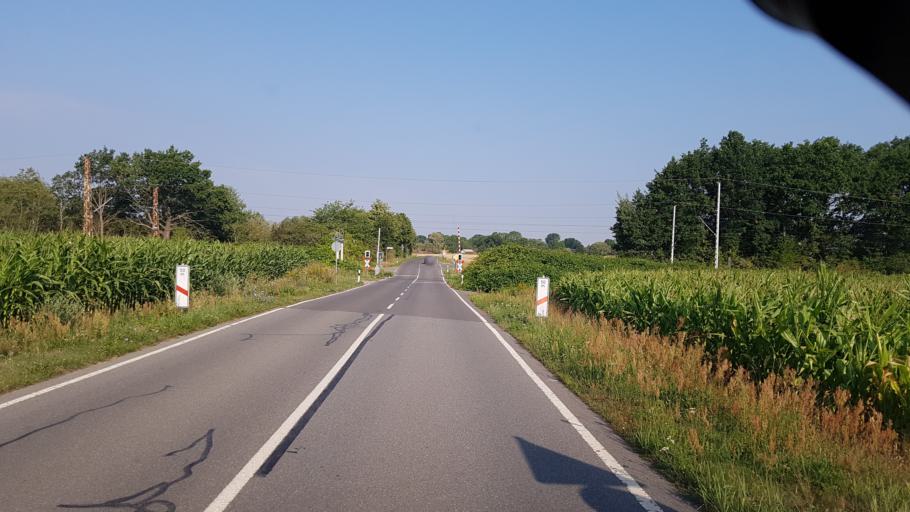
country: DE
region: Brandenburg
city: Drebkau
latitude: 51.6672
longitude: 14.2408
